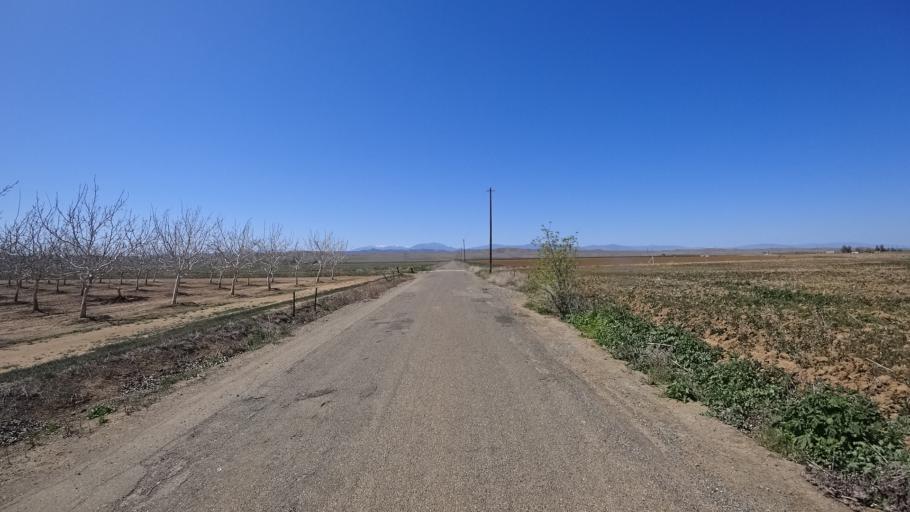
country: US
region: California
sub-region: Glenn County
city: Willows
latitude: 39.4510
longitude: -122.2671
